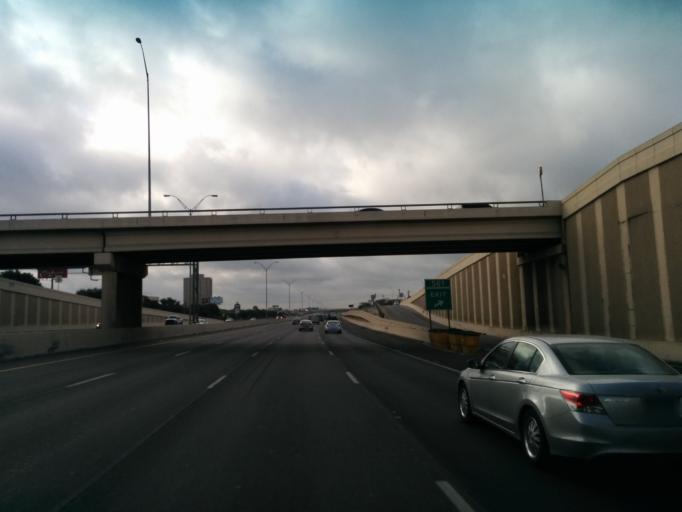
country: US
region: Texas
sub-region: Bexar County
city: Shavano Park
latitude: 29.5394
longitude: -98.5710
